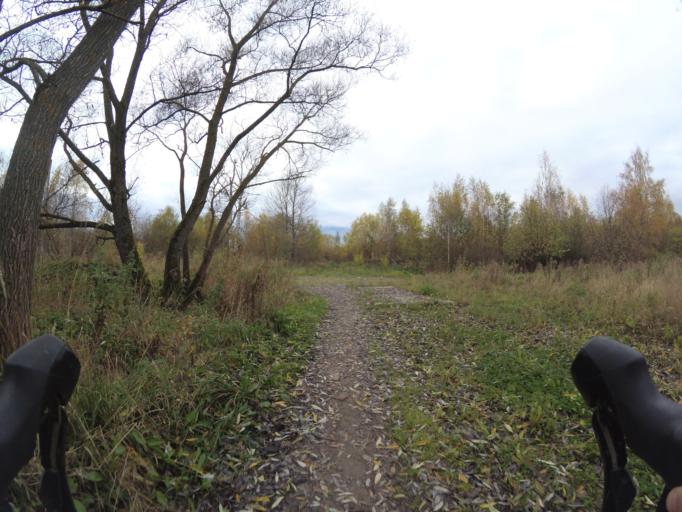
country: RU
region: St.-Petersburg
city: Lakhtinskiy
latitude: 60.0066
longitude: 30.1450
